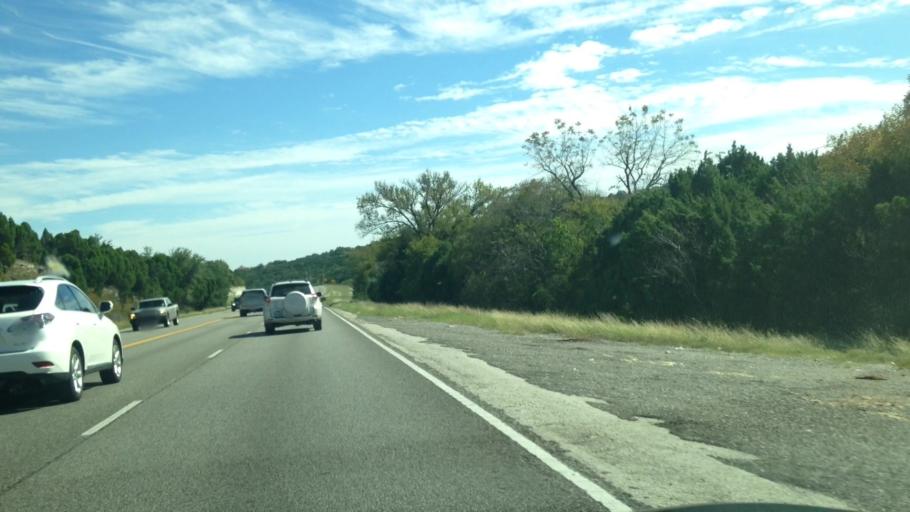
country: US
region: Texas
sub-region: Williamson County
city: Anderson Mill
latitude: 30.3858
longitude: -97.8218
